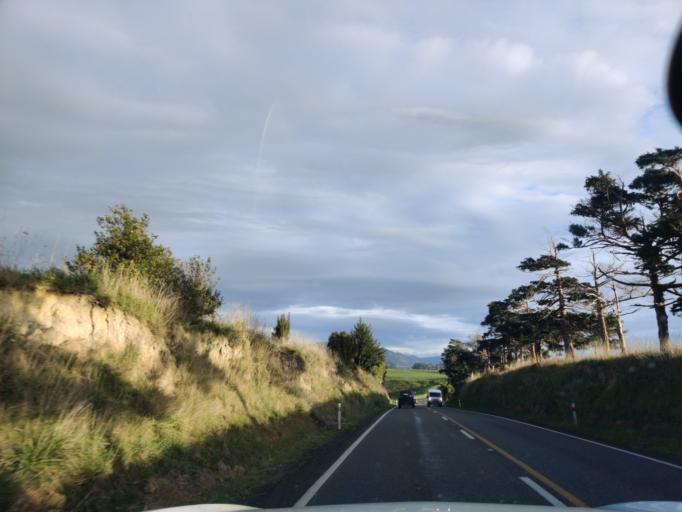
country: NZ
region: Manawatu-Wanganui
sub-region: Horowhenua District
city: Foxton
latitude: -40.5061
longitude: 175.4857
